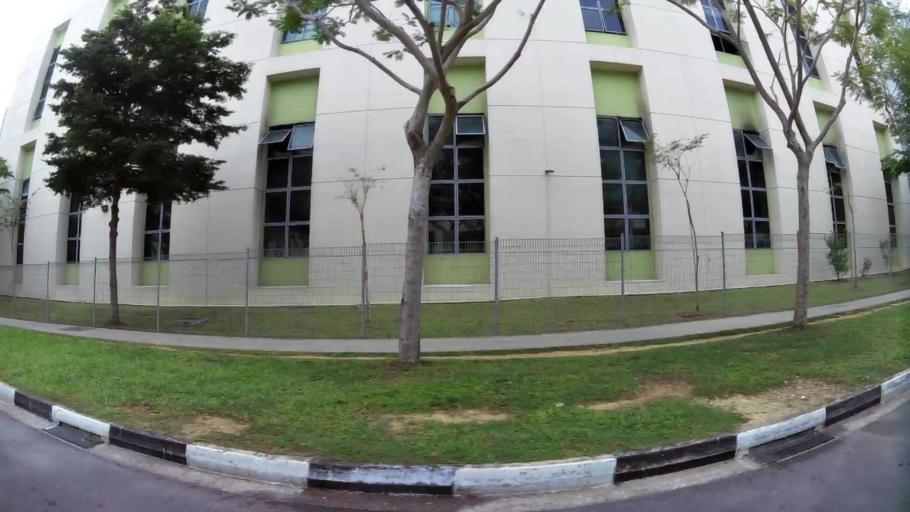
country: SG
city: Singapore
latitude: 1.3517
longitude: 103.9699
